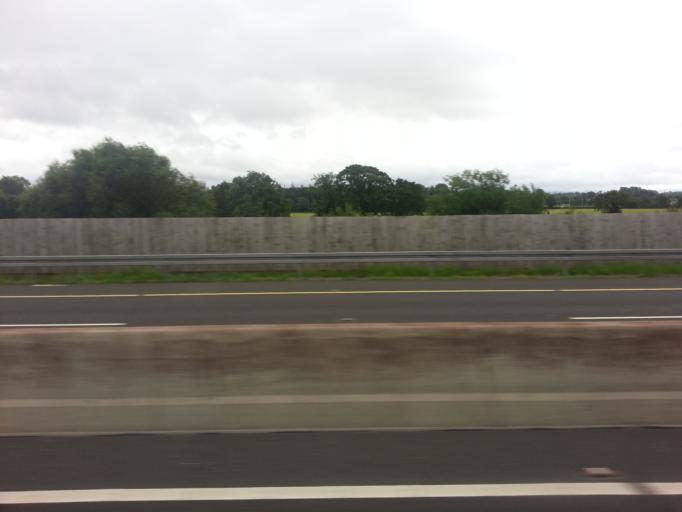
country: IE
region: Leinster
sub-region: County Carlow
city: Bagenalstown
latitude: 52.6874
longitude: -7.0317
